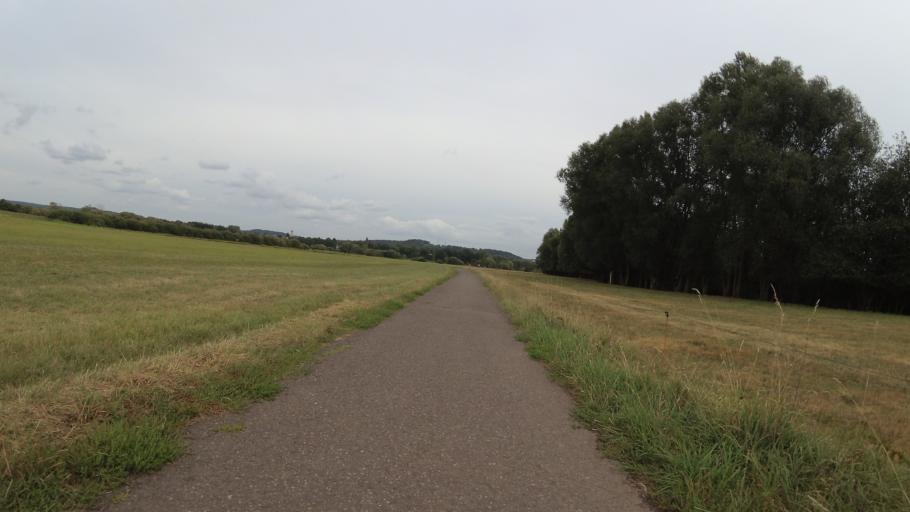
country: DE
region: Saarland
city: Homburg
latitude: 49.3099
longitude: 7.2955
